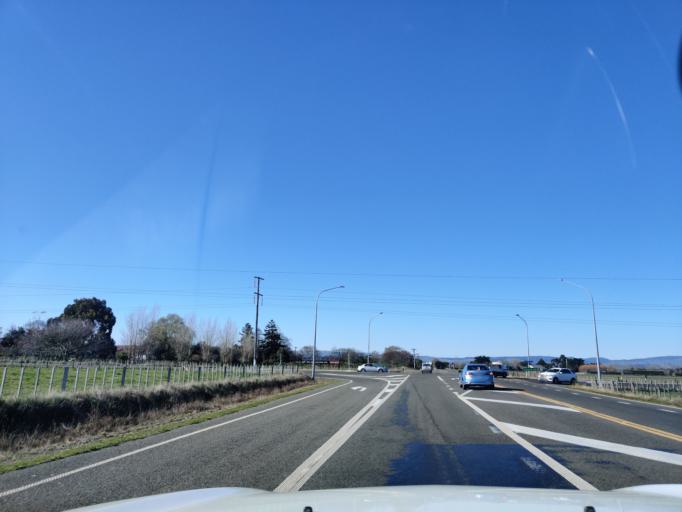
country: NZ
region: Manawatu-Wanganui
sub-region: Palmerston North City
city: Palmerston North
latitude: -40.3087
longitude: 175.5886
